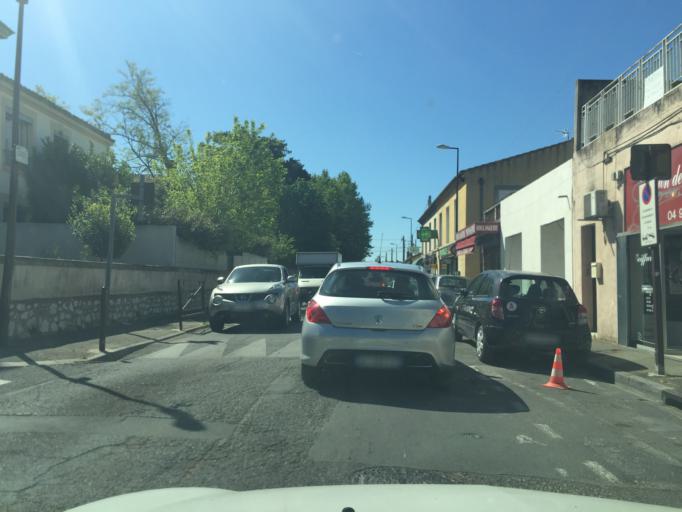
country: FR
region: Provence-Alpes-Cote d'Azur
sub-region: Departement du Vaucluse
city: Montfavet
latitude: 43.9339
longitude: 4.8724
